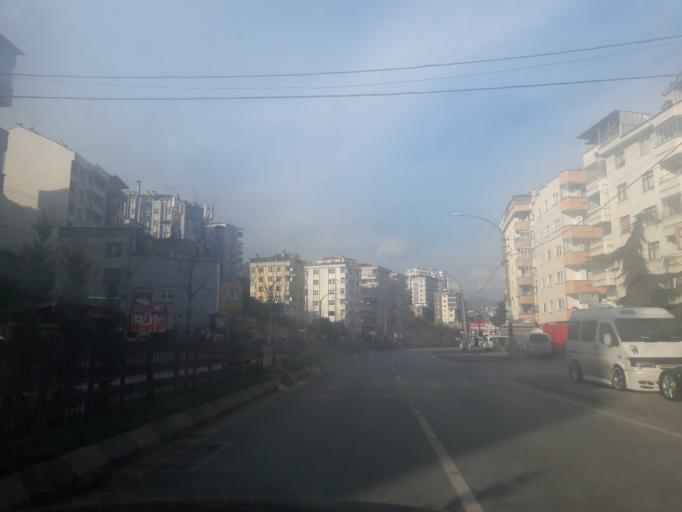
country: TR
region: Trabzon
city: Trabzon
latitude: 40.9972
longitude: 39.6889
